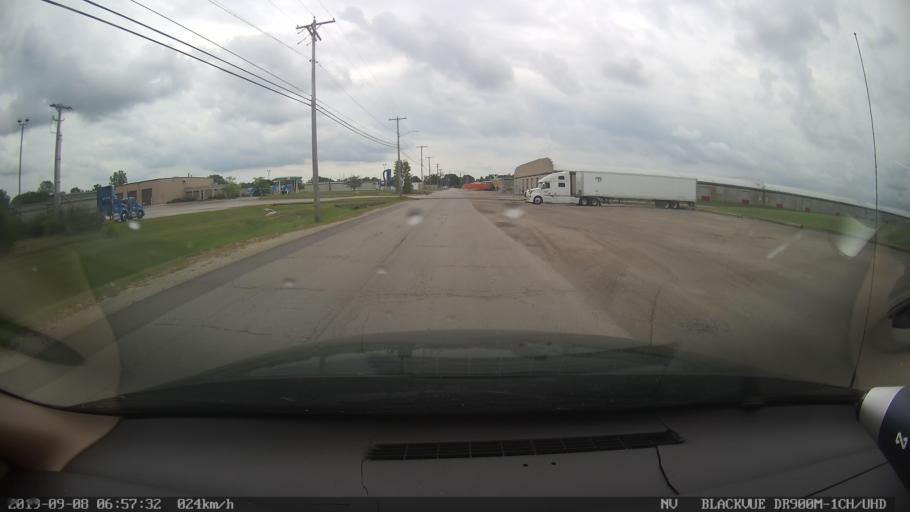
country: US
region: Ohio
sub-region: Richland County
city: Shelby
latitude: 40.9013
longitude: -82.6640
